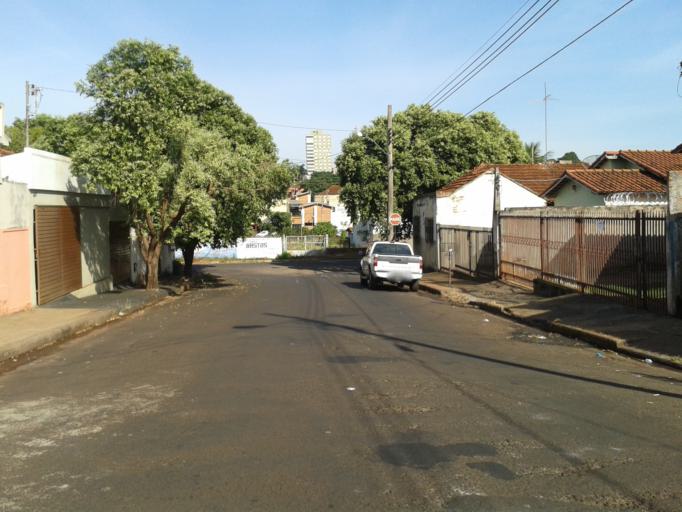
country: BR
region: Minas Gerais
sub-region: Ituiutaba
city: Ituiutaba
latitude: -18.9674
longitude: -49.4594
